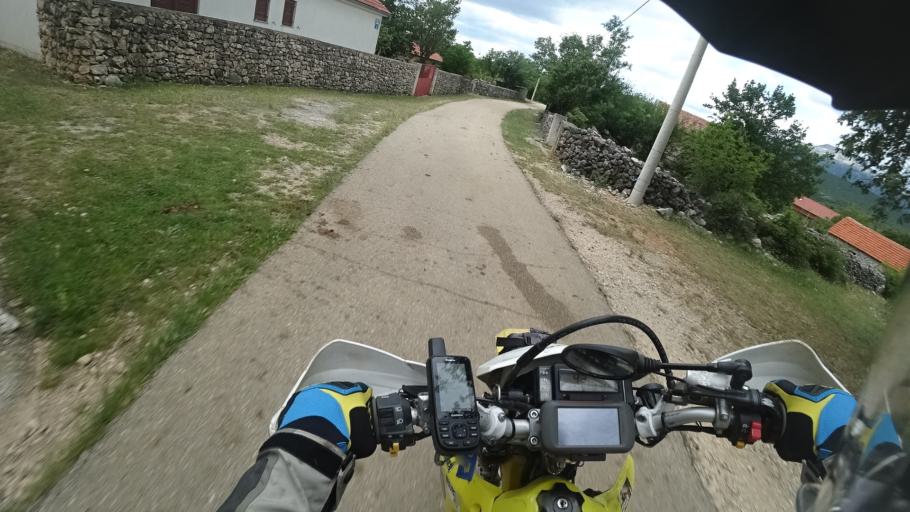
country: HR
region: Zadarska
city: Gracac
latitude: 44.1869
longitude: 15.9058
